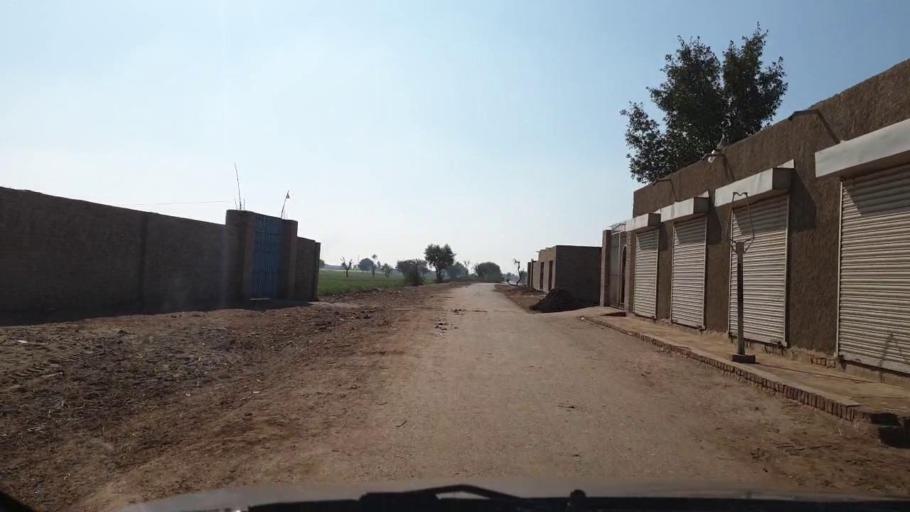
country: PK
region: Sindh
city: Sinjhoro
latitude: 25.9552
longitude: 68.7450
